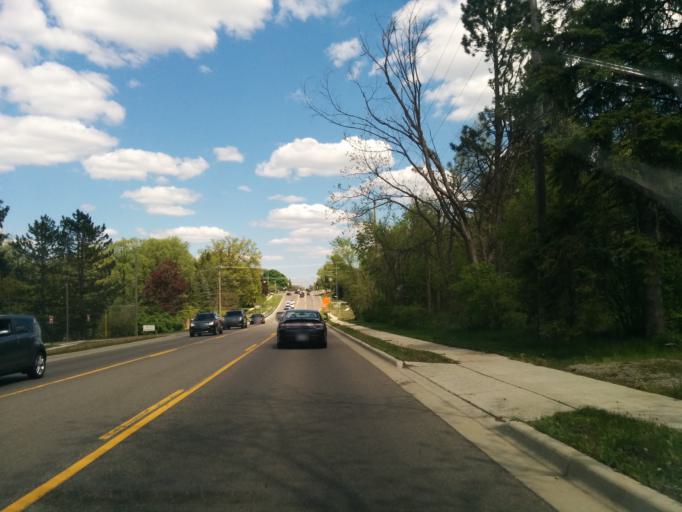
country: US
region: Michigan
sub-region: Oakland County
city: Franklin
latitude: 42.5141
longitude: -83.3441
